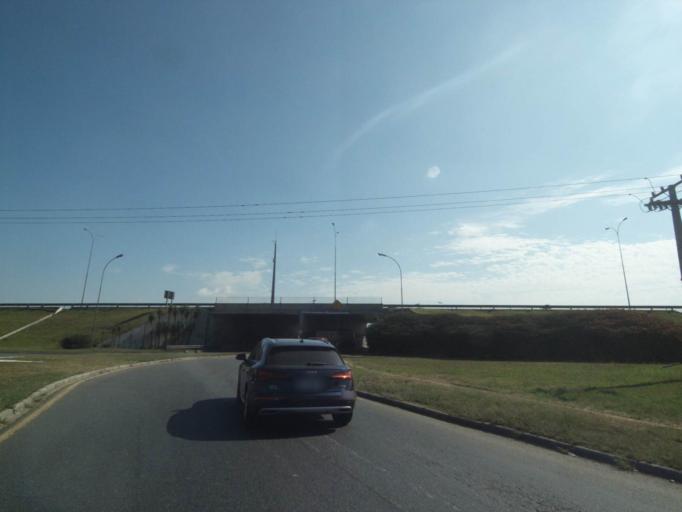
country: BR
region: Parana
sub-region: Sao Jose Dos Pinhais
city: Sao Jose dos Pinhais
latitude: -25.4965
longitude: -49.1630
